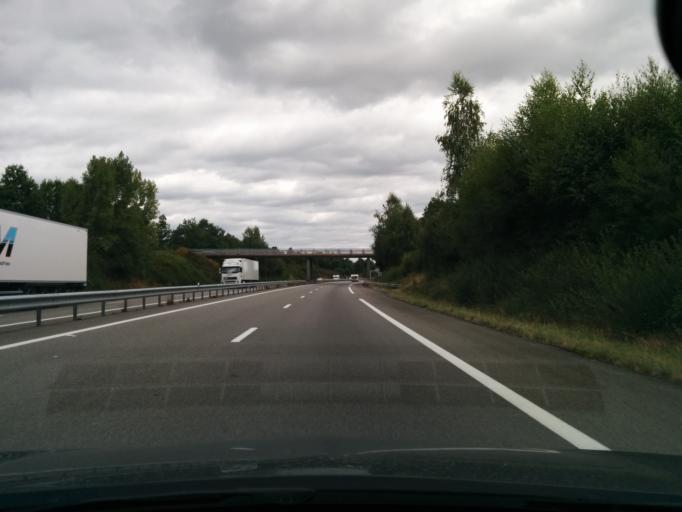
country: FR
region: Limousin
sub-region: Departement de la Haute-Vienne
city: Saint-Sulpice-les-Feuilles
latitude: 46.3538
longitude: 1.4269
